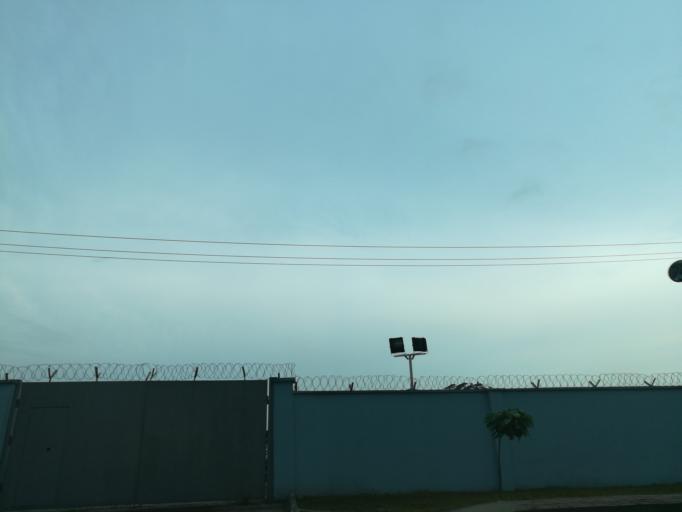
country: NG
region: Rivers
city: Port Harcourt
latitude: 4.8160
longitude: 7.0307
